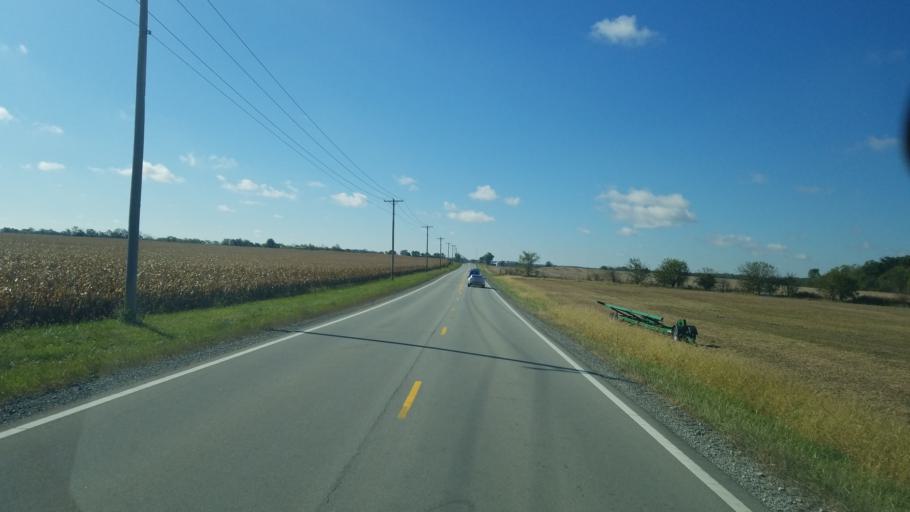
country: US
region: Ohio
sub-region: Highland County
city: Leesburg
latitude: 39.4153
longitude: -83.5234
